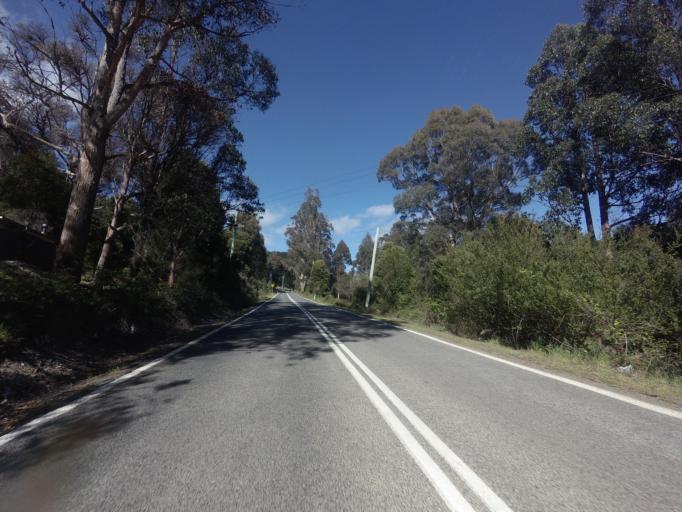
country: AU
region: Tasmania
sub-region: Derwent Valley
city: New Norfolk
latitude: -42.7058
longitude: 146.7119
